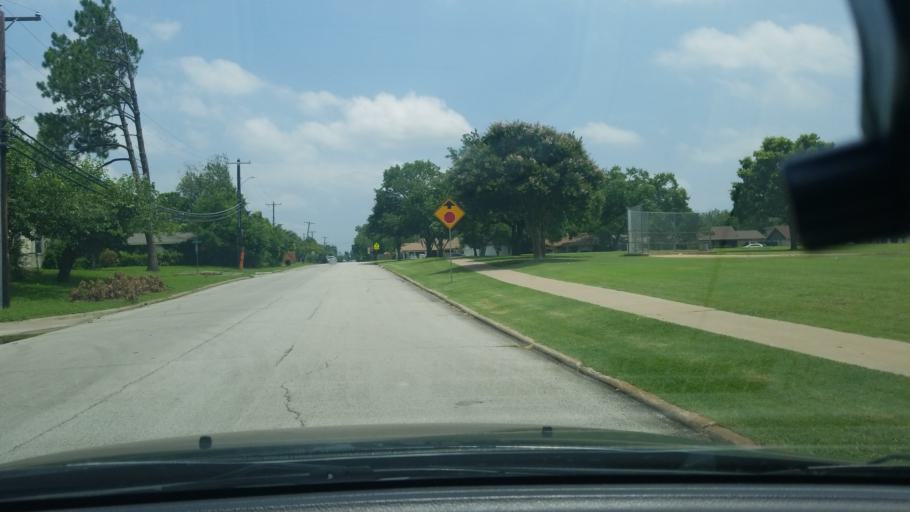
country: US
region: Texas
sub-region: Dallas County
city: Mesquite
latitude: 32.7980
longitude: -96.6439
